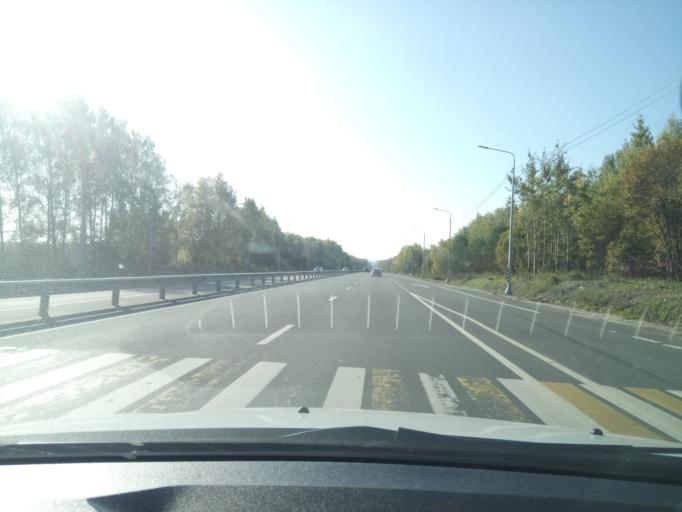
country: RU
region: Nizjnij Novgorod
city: Burevestnik
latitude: 56.0344
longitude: 43.9611
